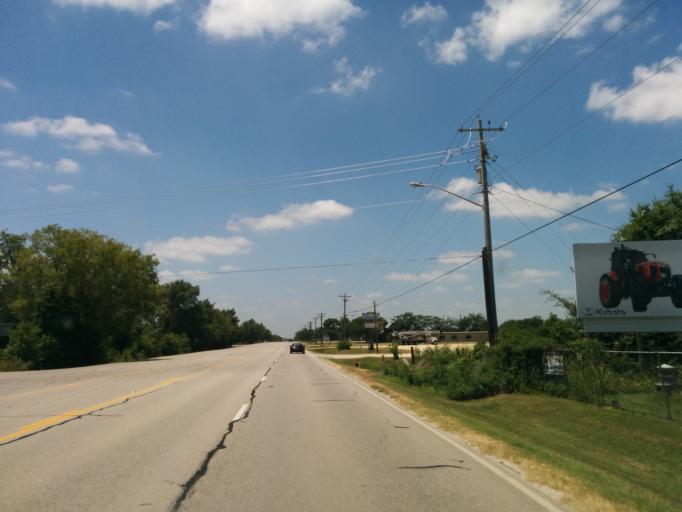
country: US
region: Texas
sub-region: Brazos County
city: Bryan
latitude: 30.7182
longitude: -96.3396
